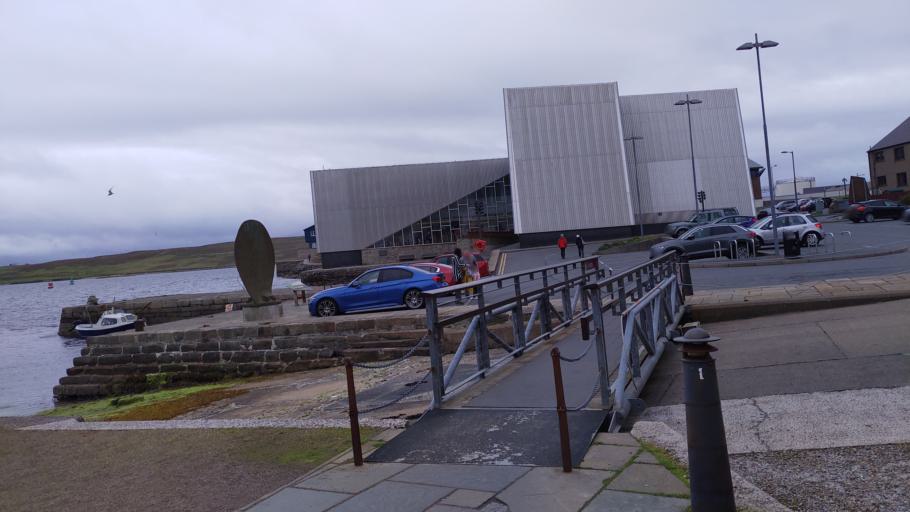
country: GB
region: Scotland
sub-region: Shetland Islands
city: Lerwick
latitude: 60.1580
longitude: -1.1495
